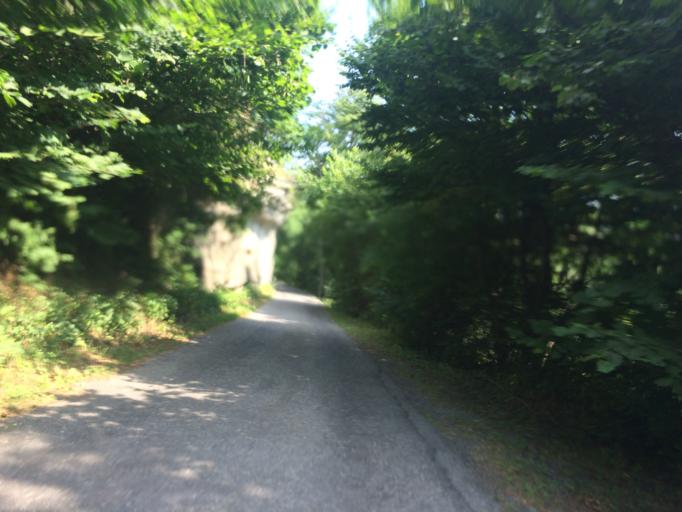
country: IT
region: Liguria
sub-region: Provincia di Savona
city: Giusvalla
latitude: 44.4611
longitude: 8.3552
